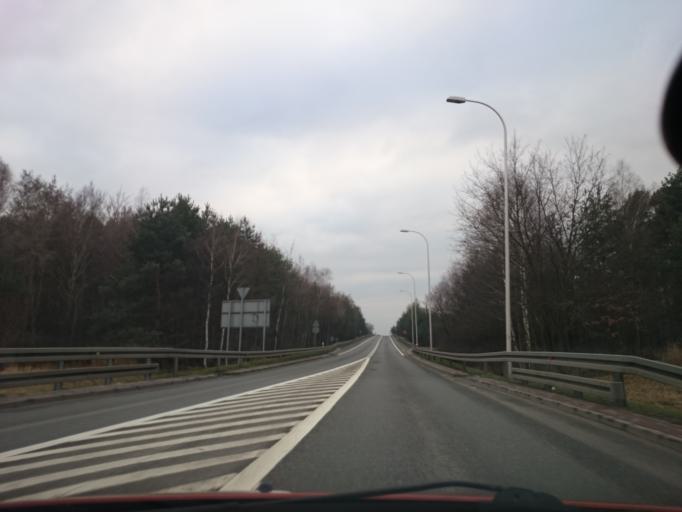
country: PL
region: Opole Voivodeship
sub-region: Powiat opolski
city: Dabrowa
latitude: 50.6648
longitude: 17.6985
